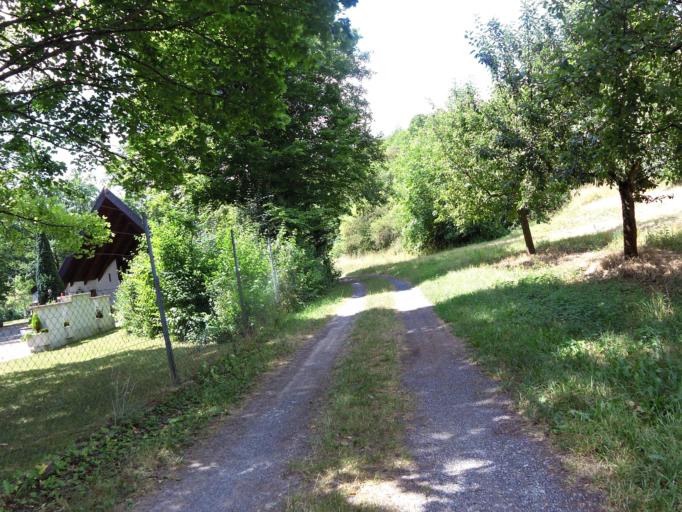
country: DE
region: Bavaria
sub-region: Regierungsbezirk Unterfranken
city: Gerbrunn
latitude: 49.7801
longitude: 9.9932
